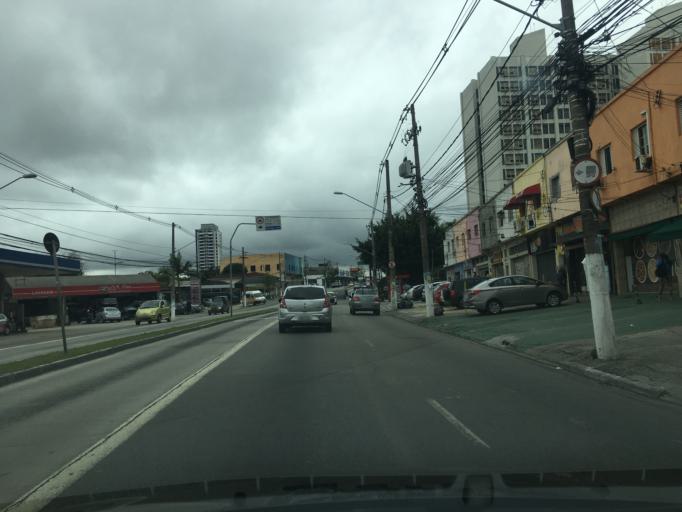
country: BR
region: Sao Paulo
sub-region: Taboao Da Serra
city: Taboao da Serra
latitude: -23.5856
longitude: -46.7215
